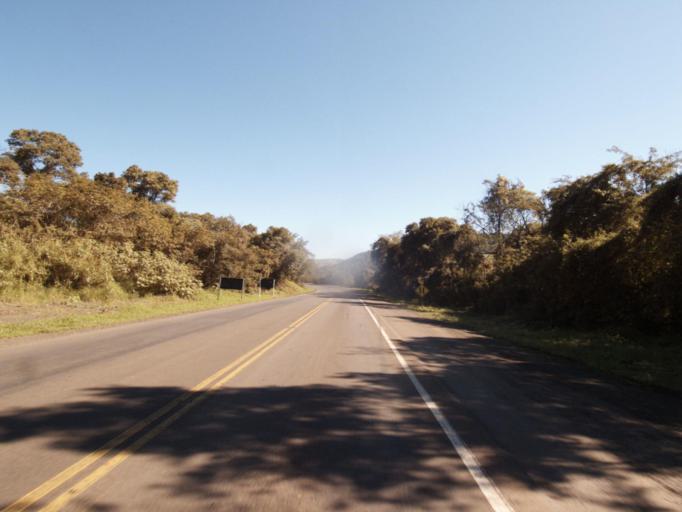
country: BR
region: Rio Grande do Sul
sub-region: Frederico Westphalen
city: Frederico Westphalen
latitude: -26.8205
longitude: -53.3804
